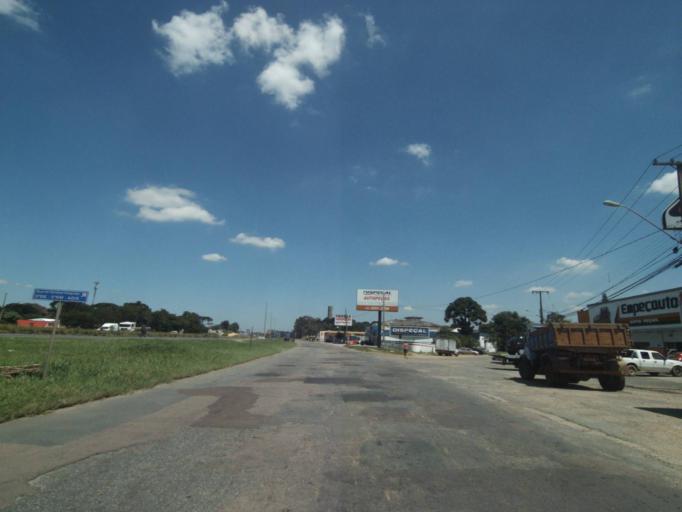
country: BR
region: Parana
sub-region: Sao Jose Dos Pinhais
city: Sao Jose dos Pinhais
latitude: -25.5275
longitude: -49.2985
